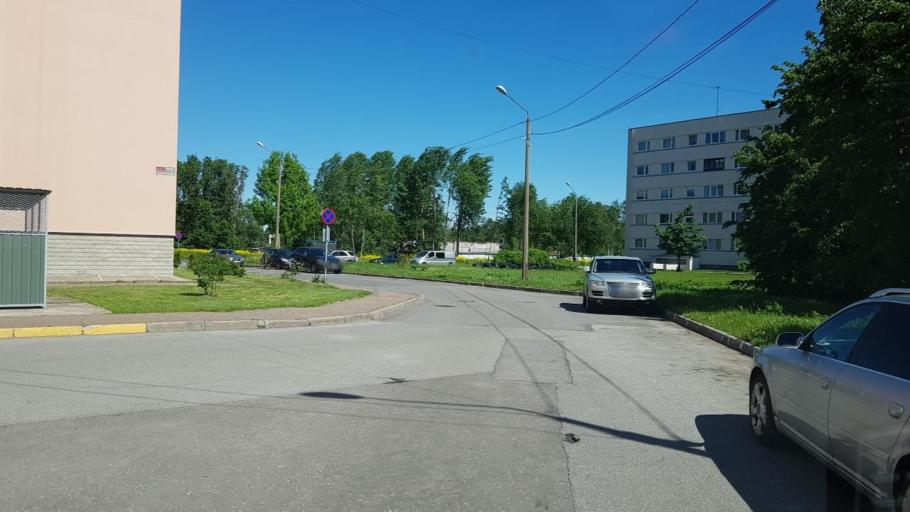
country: EE
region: Ida-Virumaa
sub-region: Narva linn
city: Narva
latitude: 59.3921
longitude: 28.1766
